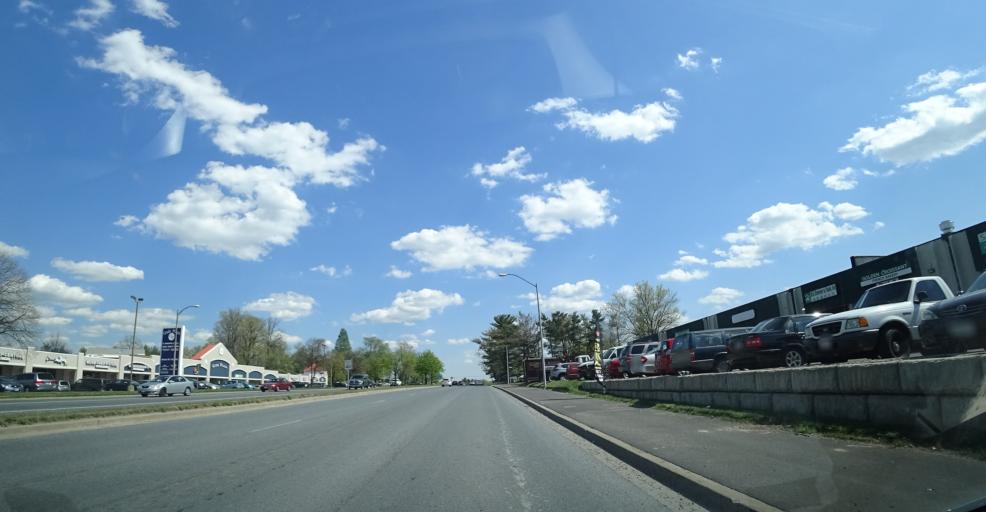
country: US
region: Maryland
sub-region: Montgomery County
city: Rockville
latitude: 39.0973
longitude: -77.1361
